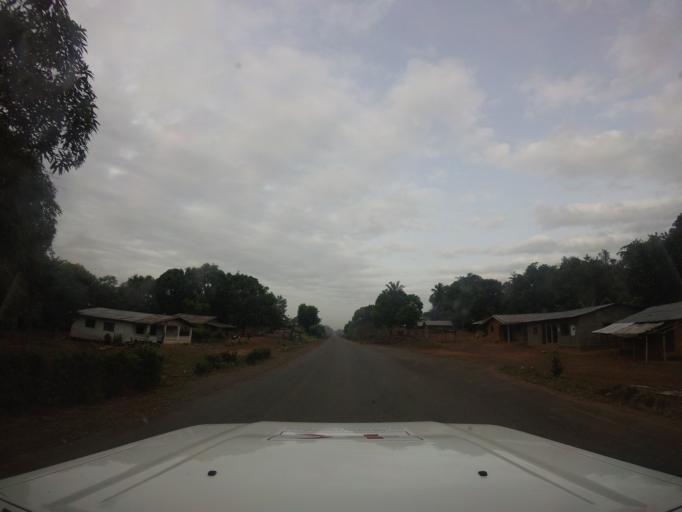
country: LR
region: Bomi
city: Tubmanburg
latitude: 6.7320
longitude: -10.9968
